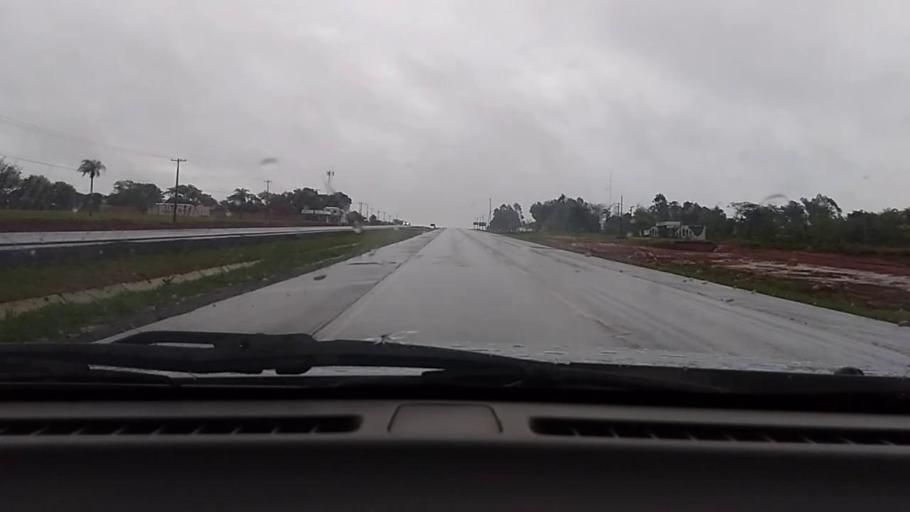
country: PY
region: Caaguazu
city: Caaguazu
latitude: -25.4653
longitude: -55.9602
